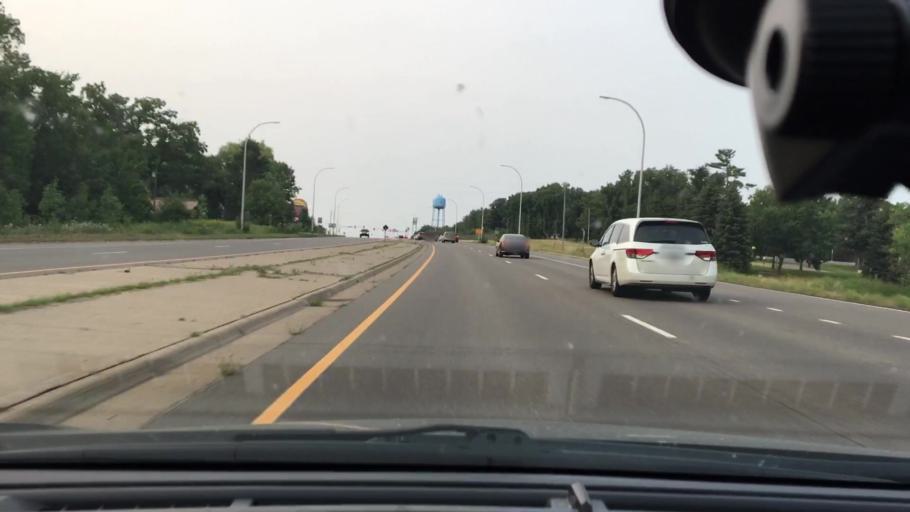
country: US
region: Minnesota
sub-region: Mille Lacs County
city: Vineland
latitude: 46.1762
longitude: -93.7568
